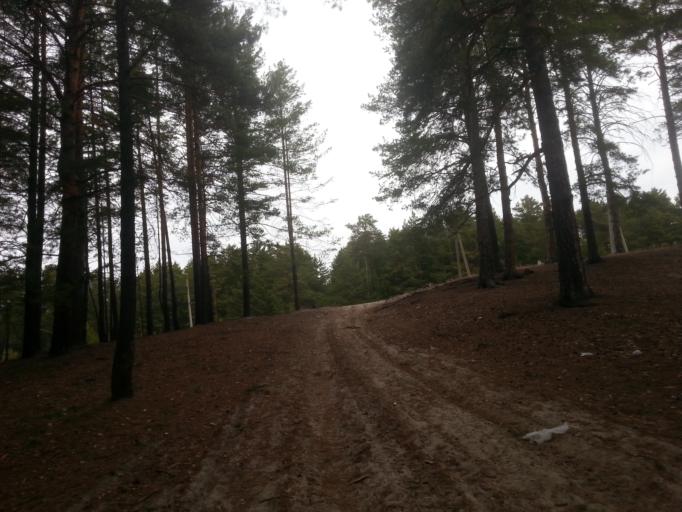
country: RU
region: Altai Krai
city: Yuzhnyy
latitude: 53.3141
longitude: 83.6900
